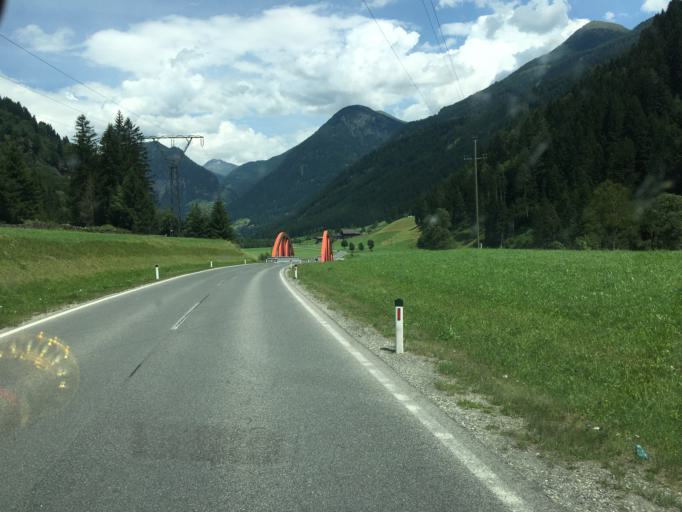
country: AT
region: Carinthia
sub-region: Politischer Bezirk Spittal an der Drau
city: Winklern
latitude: 46.8857
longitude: 12.8908
